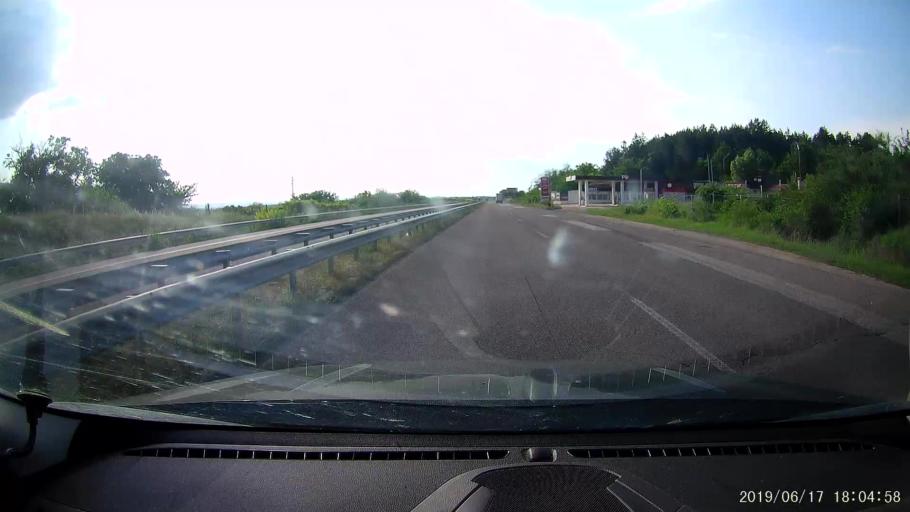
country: BG
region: Khaskovo
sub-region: Obshtina Svilengrad
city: Svilengrad
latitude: 41.7922
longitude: 26.1863
